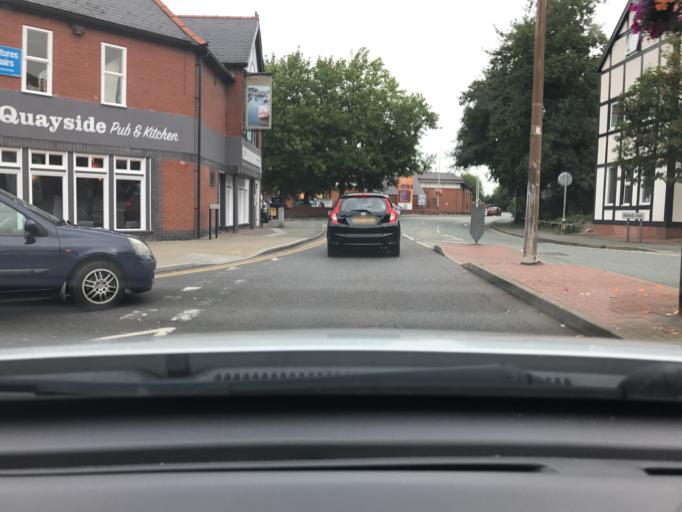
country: GB
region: England
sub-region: Cheshire West and Chester
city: Marston
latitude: 53.2621
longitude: -2.5079
